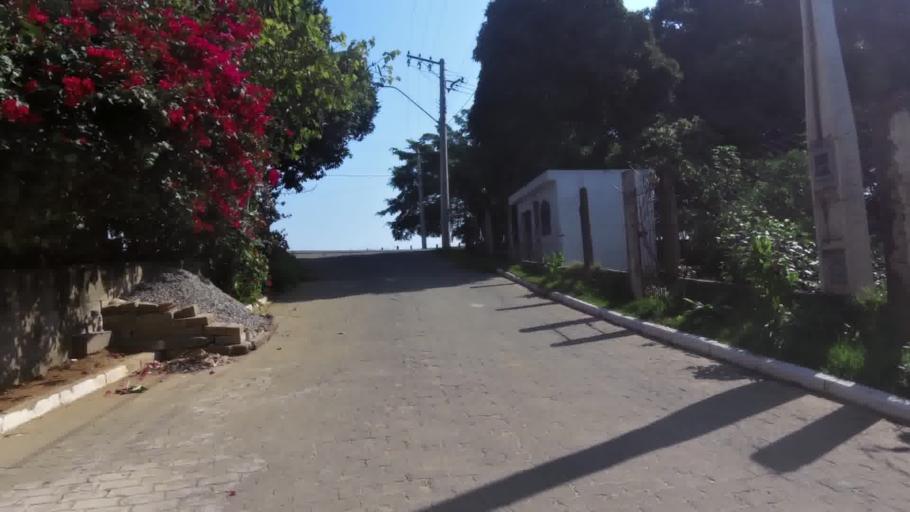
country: BR
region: Espirito Santo
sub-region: Piuma
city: Piuma
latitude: -20.8086
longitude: -40.7389
